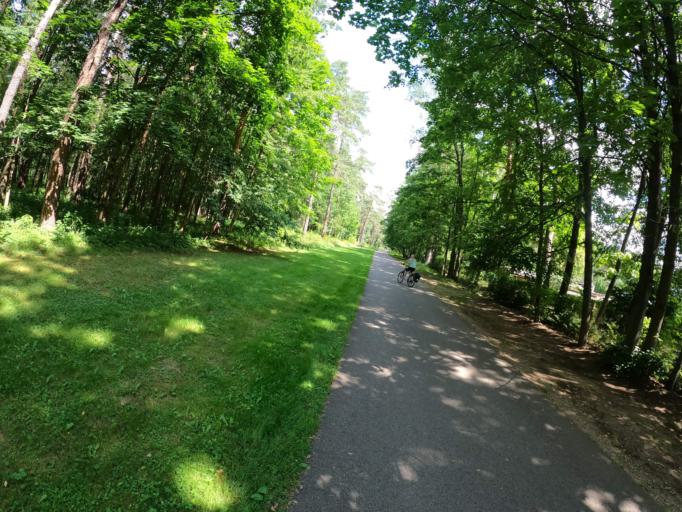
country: LT
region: Alytaus apskritis
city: Druskininkai
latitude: 54.0194
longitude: 23.9916
